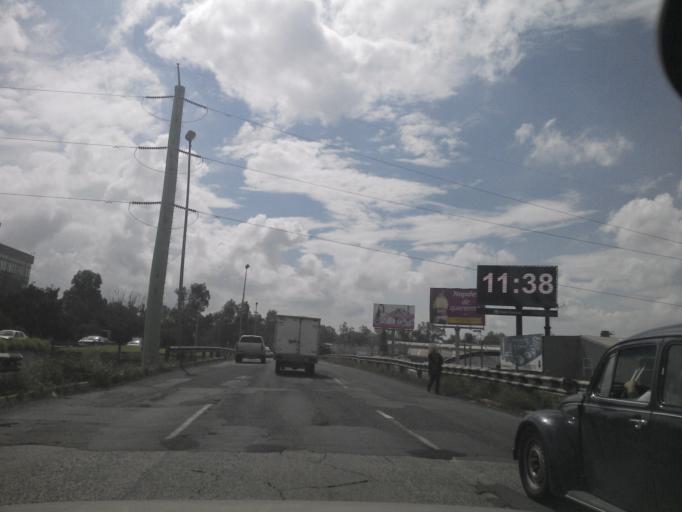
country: MX
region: Jalisco
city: Tlaquepaque
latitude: 20.6369
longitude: -103.3431
